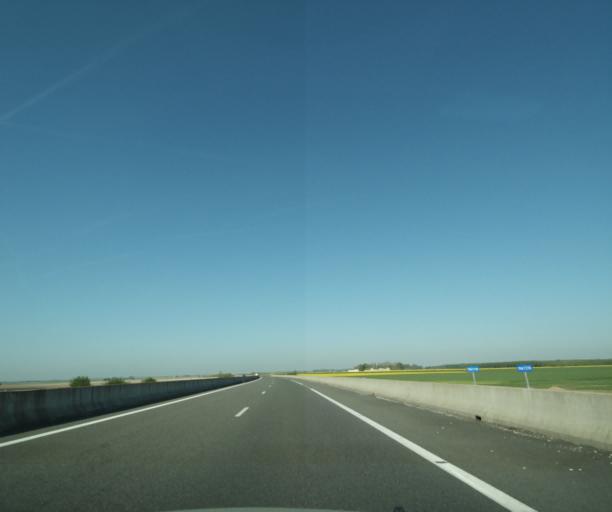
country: FR
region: Centre
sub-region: Departement du Loiret
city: Corbeilles
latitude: 48.0957
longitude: 2.5668
